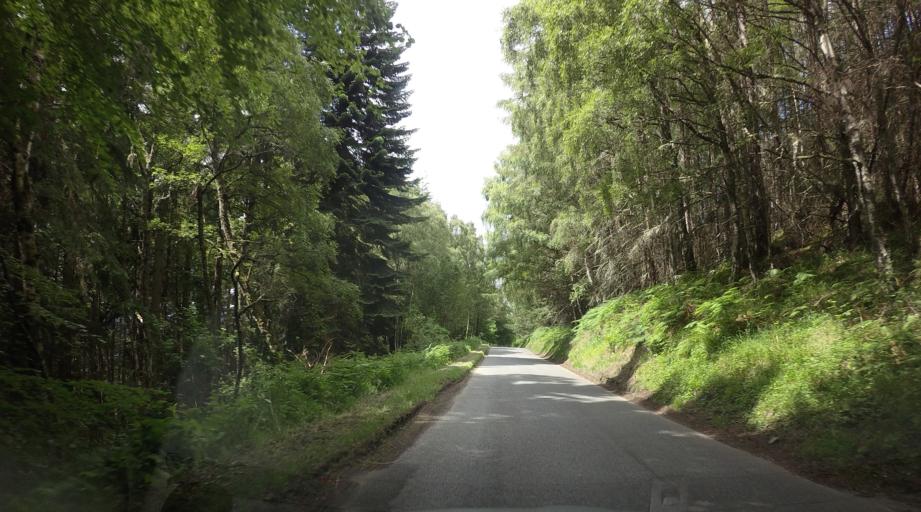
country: GB
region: Scotland
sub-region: Perth and Kinross
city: Aberfeldy
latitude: 56.7186
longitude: -3.8827
